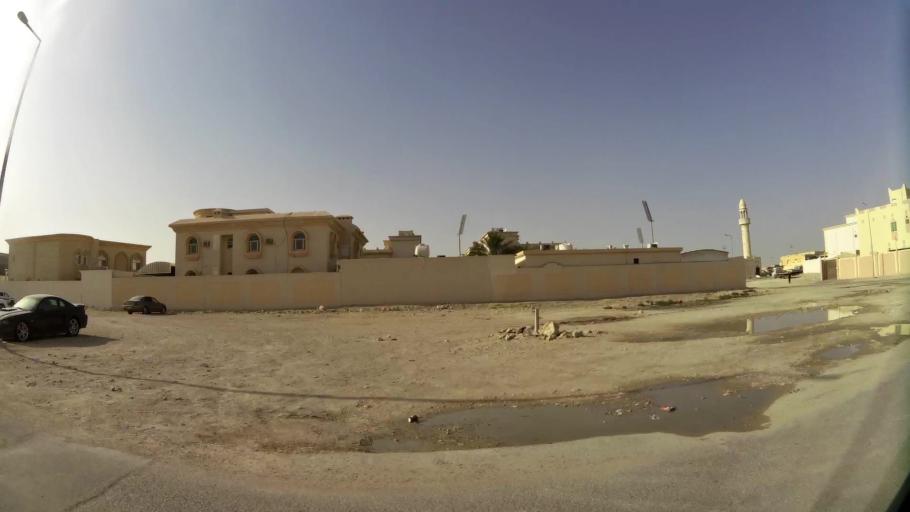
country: QA
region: Baladiyat ar Rayyan
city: Ar Rayyan
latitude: 25.3409
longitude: 51.4407
